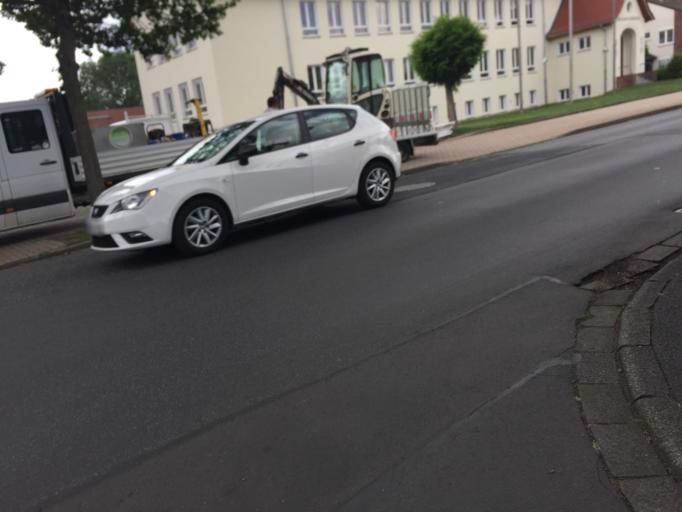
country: DE
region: Hesse
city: Schwalmstadt
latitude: 50.9139
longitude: 9.2396
